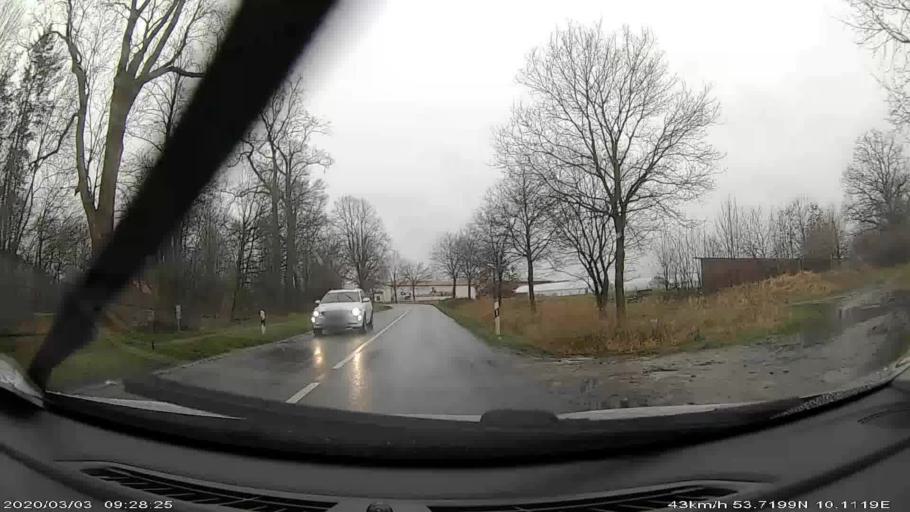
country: DE
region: Hamburg
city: Duvenstedt
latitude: 53.7165
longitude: 10.1109
